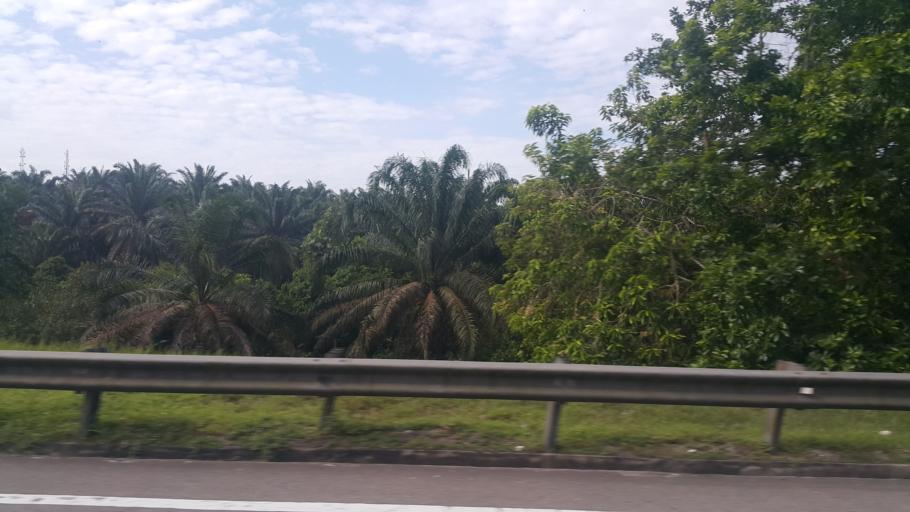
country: MY
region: Johor
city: Taman Senai
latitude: 1.6083
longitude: 103.6122
